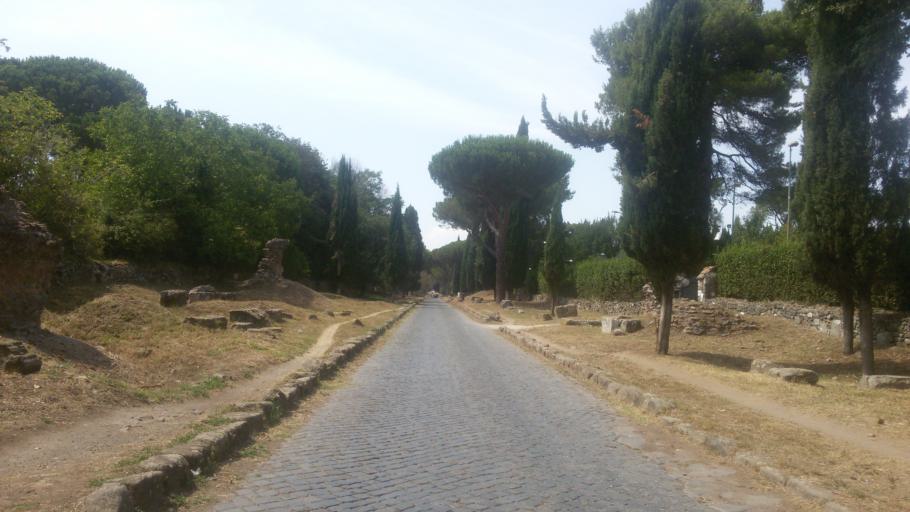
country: IT
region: Latium
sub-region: Citta metropolitana di Roma Capitale
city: Rome
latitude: 41.8323
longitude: 12.5428
